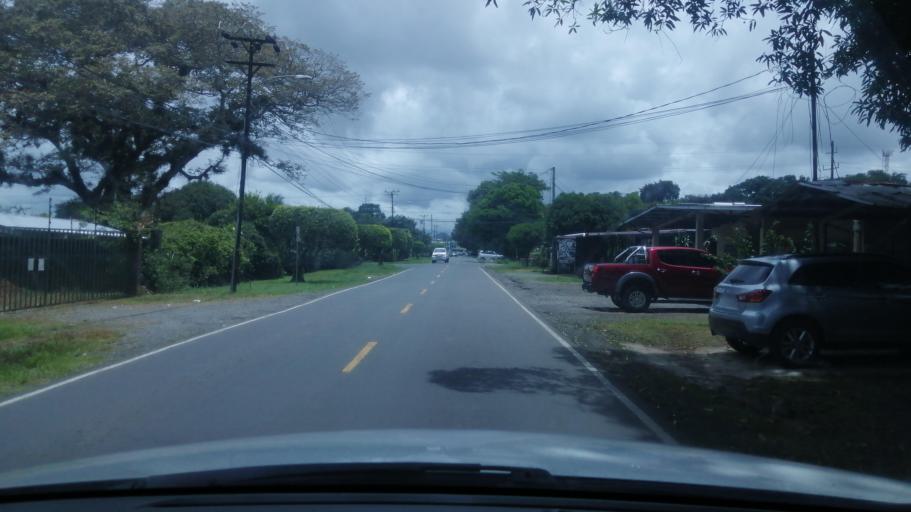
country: PA
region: Chiriqui
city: David
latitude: 8.4405
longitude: -82.4296
